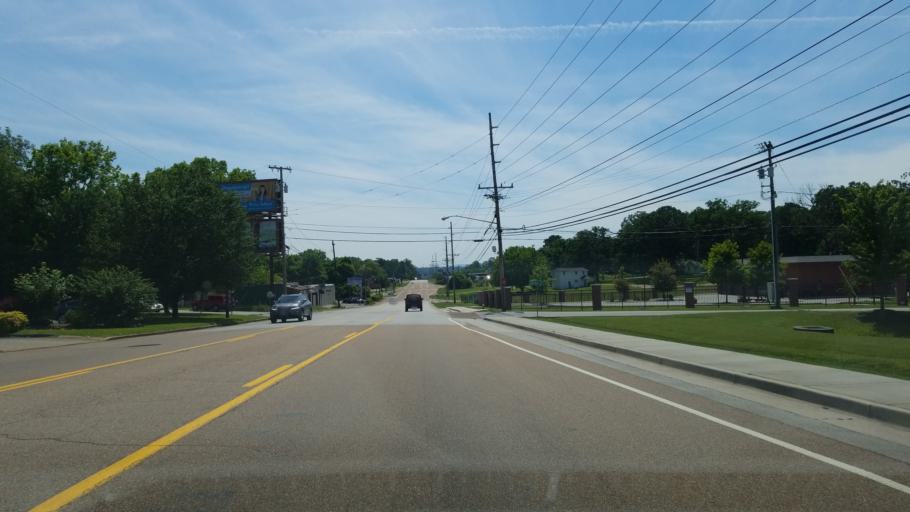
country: US
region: Tennessee
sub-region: Hamilton County
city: Harrison
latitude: 35.0583
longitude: -85.1378
